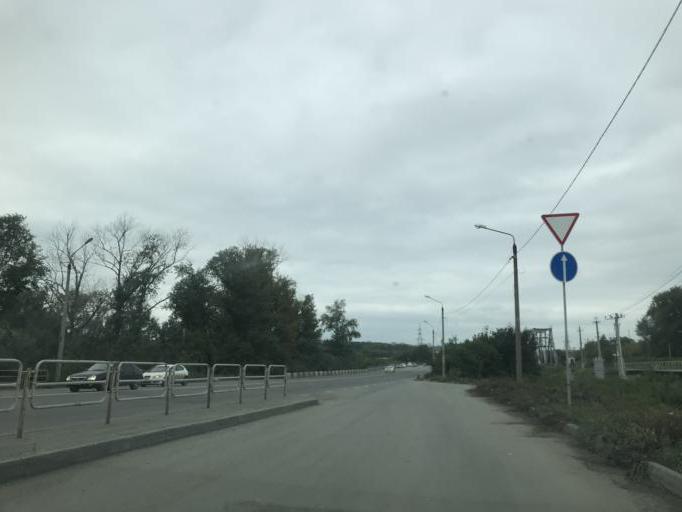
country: RU
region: Chelyabinsk
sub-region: Gorod Chelyabinsk
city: Chelyabinsk
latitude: 55.1988
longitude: 61.4060
